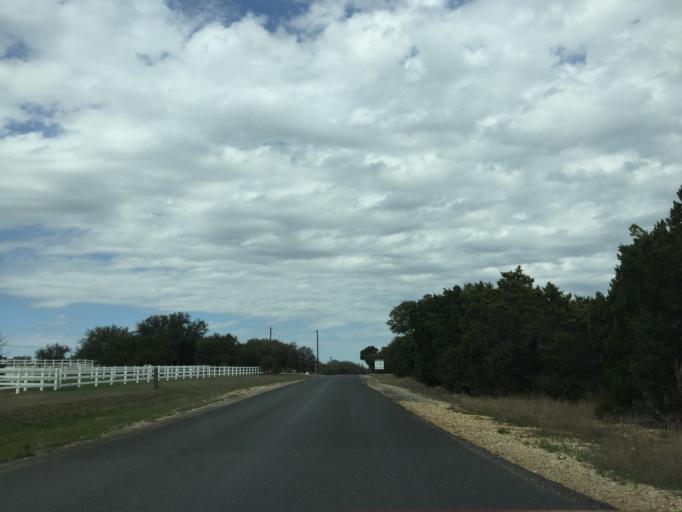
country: US
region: Texas
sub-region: Burnet County
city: Bertram
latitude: 30.7291
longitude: -97.9342
